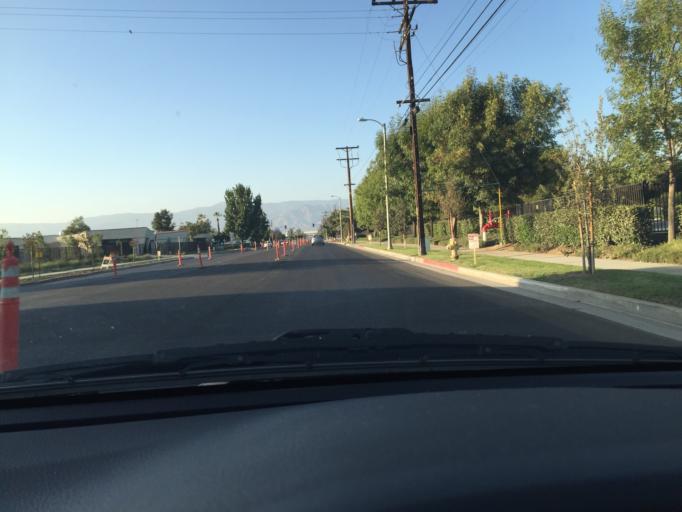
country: US
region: California
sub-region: San Bernardino County
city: Redlands
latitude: 34.0535
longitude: -117.2000
